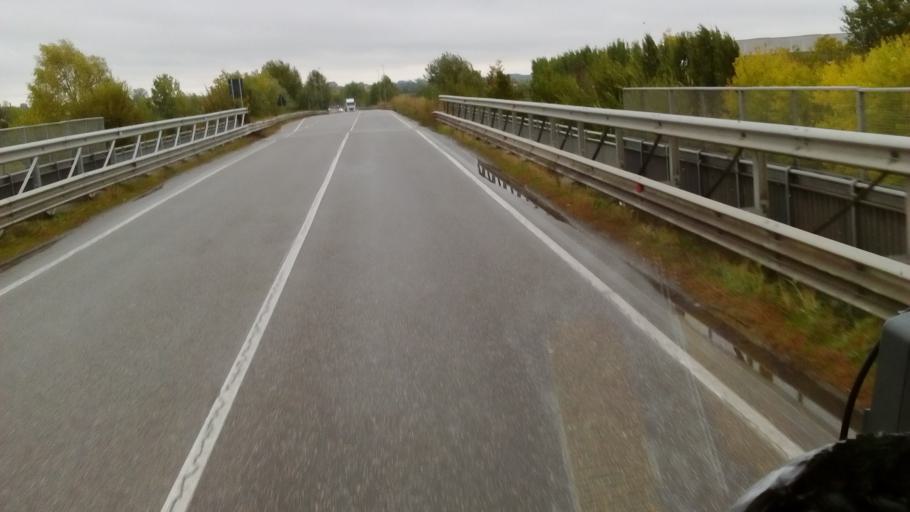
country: IT
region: Emilia-Romagna
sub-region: Provincia di Reggio Emilia
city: Luzzara
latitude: 44.9460
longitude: 10.7124
